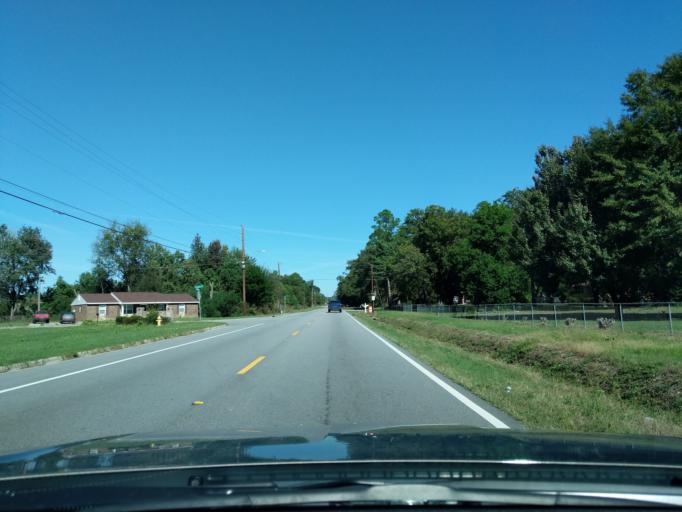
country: US
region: Georgia
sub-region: Richmond County
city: Hephzibah
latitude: 33.3597
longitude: -81.9972
